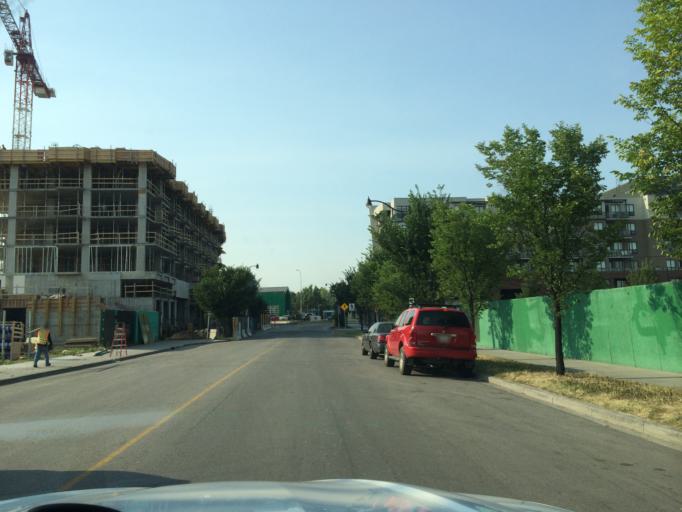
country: CA
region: Alberta
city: Calgary
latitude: 51.0507
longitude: -114.0404
